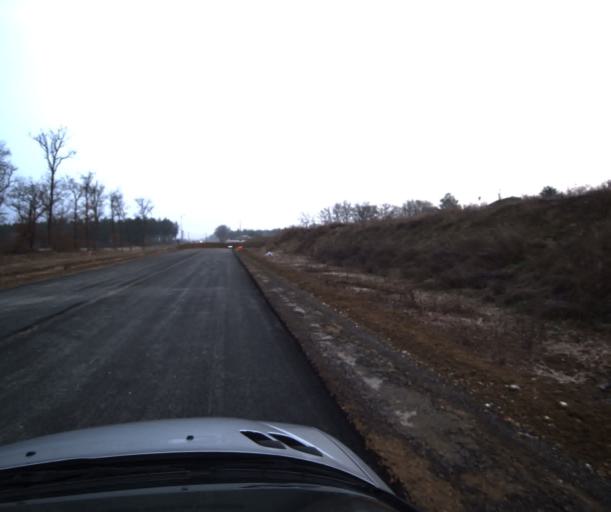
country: FR
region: Midi-Pyrenees
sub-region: Departement de la Haute-Garonne
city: Fontenilles
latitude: 43.5688
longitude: 1.1981
